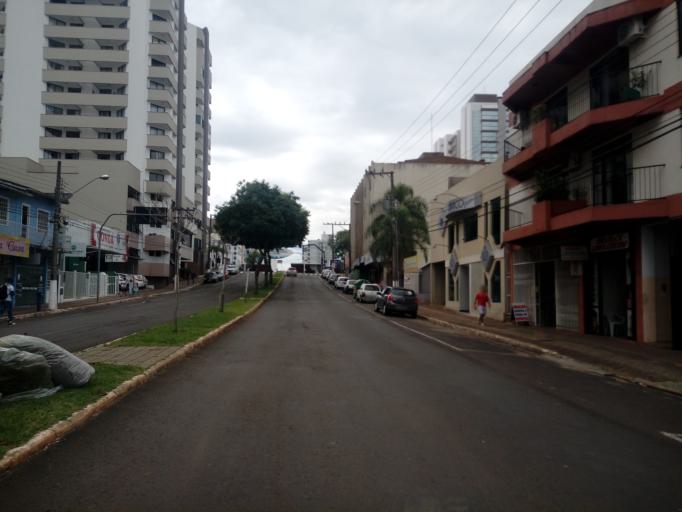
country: BR
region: Santa Catarina
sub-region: Chapeco
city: Chapeco
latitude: -27.1069
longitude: -52.6151
